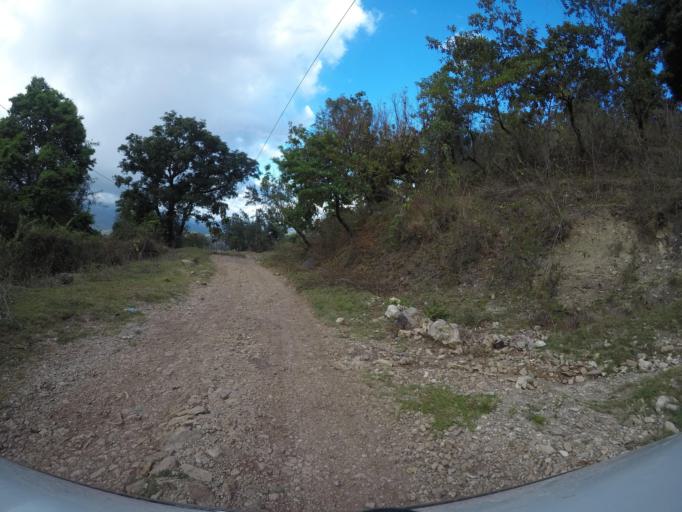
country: TL
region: Baucau
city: Venilale
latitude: -8.6870
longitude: 126.6628
